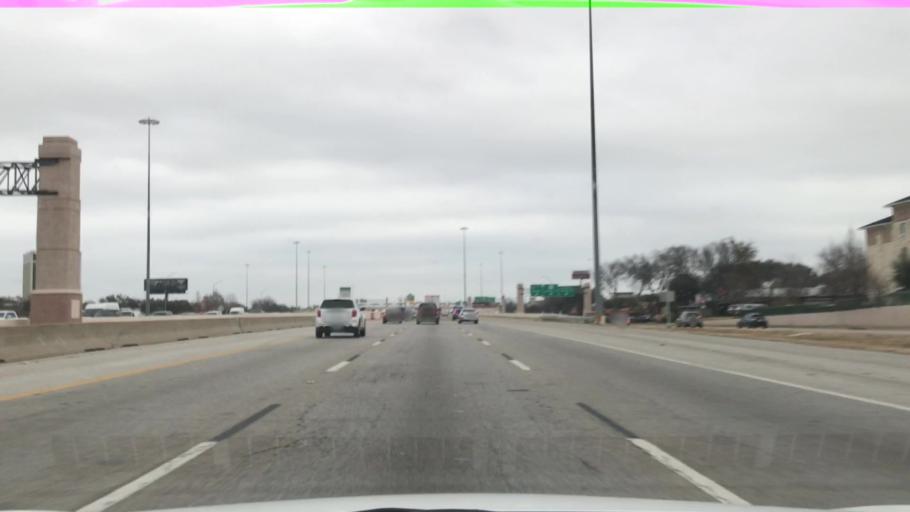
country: US
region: Texas
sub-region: Tarrant County
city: Arlington
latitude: 32.7596
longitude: -97.1114
